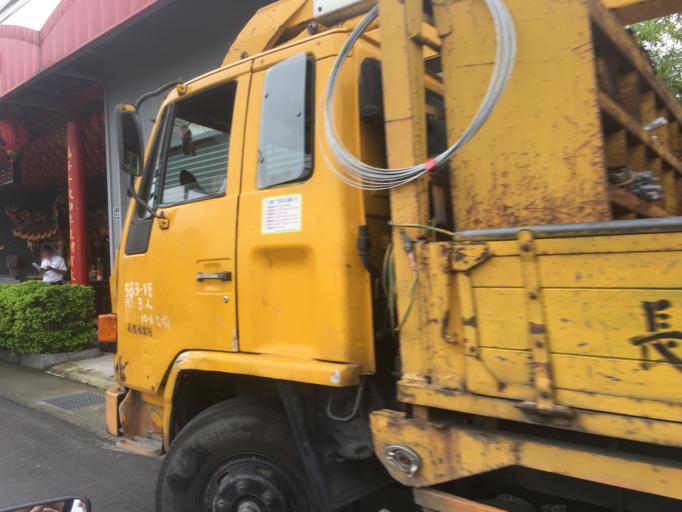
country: TW
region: Taiwan
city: Zhongxing New Village
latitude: 24.0508
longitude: 120.6848
